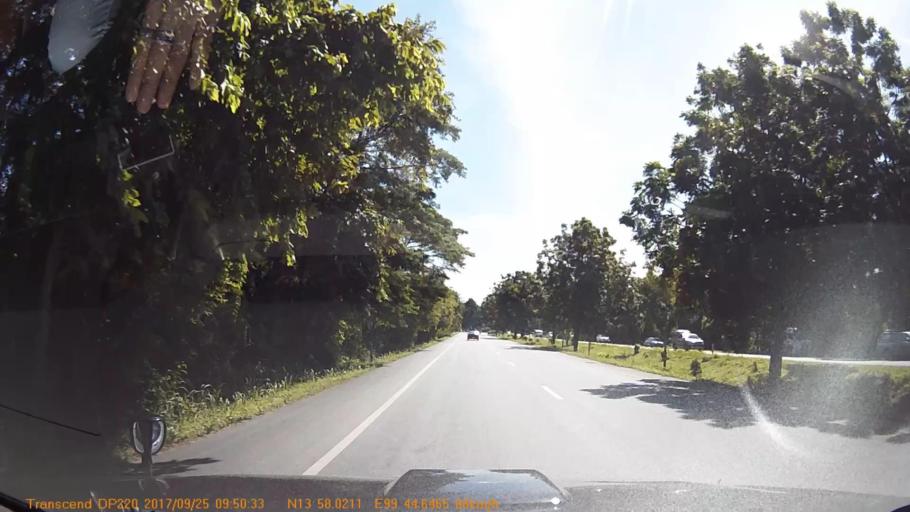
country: TH
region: Kanchanaburi
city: Tha Maka
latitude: 13.9671
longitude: 99.7445
